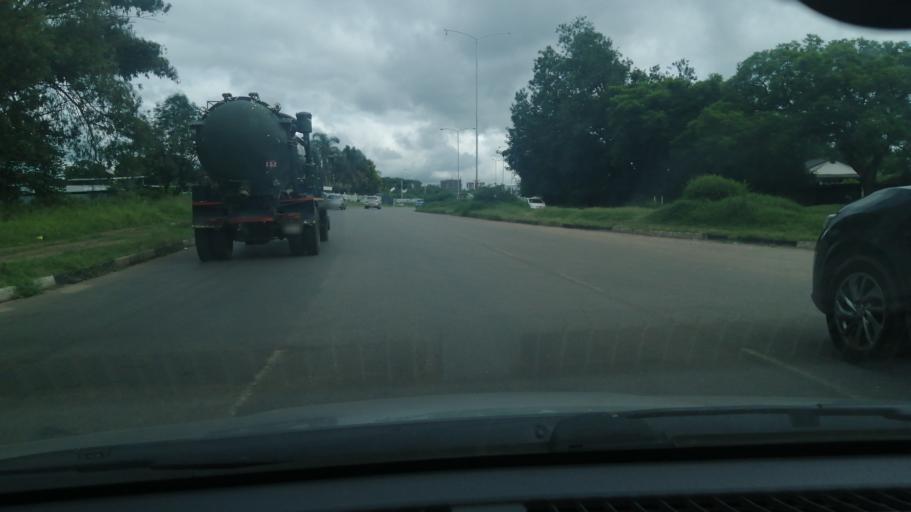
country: ZW
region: Harare
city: Harare
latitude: -17.8283
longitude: 31.0611
